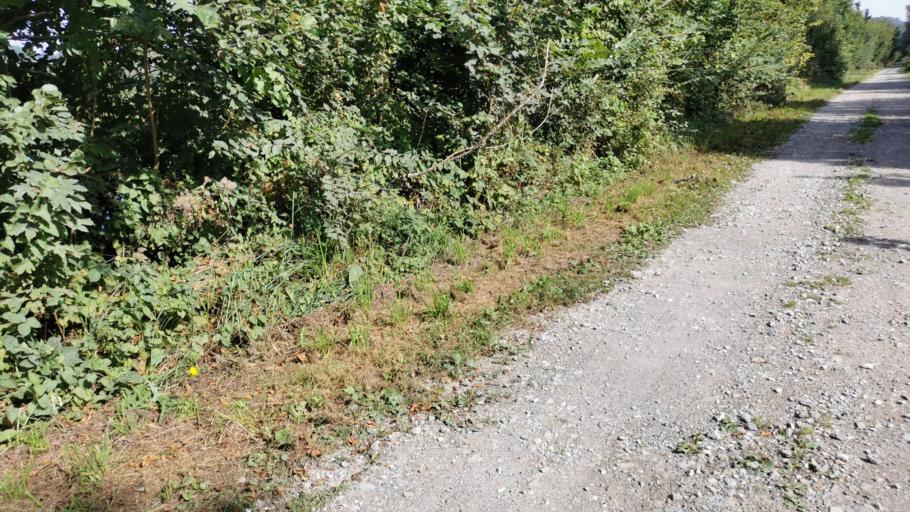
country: FR
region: Picardie
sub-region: Departement de la Somme
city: Longpre-les-Corps-Saints
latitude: 50.0347
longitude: 1.9575
